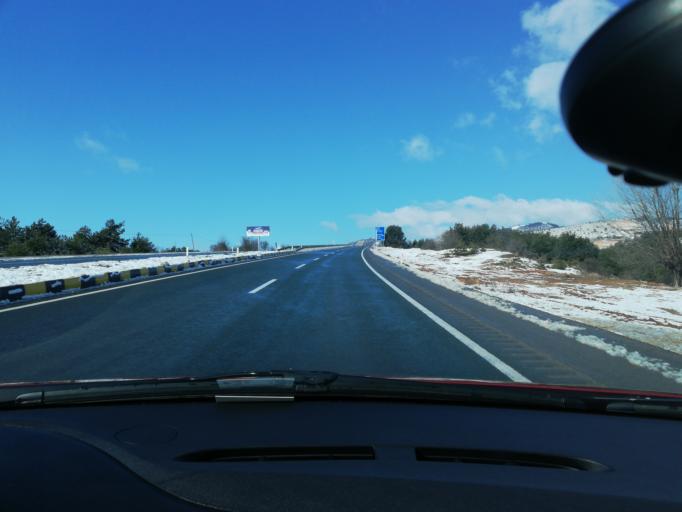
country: TR
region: Kastamonu
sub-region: Cide
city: Kastamonu
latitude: 41.3643
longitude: 33.7363
